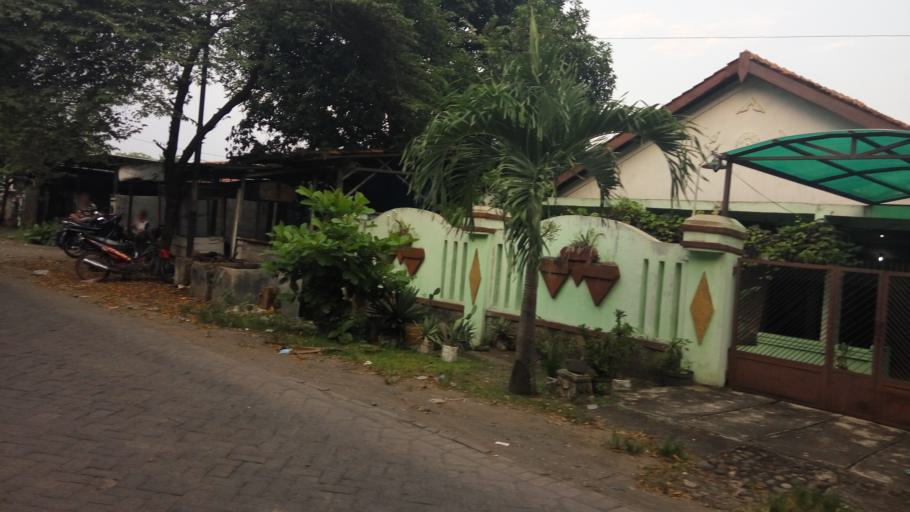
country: ID
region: Central Java
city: Semarang
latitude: -7.0160
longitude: 110.3840
